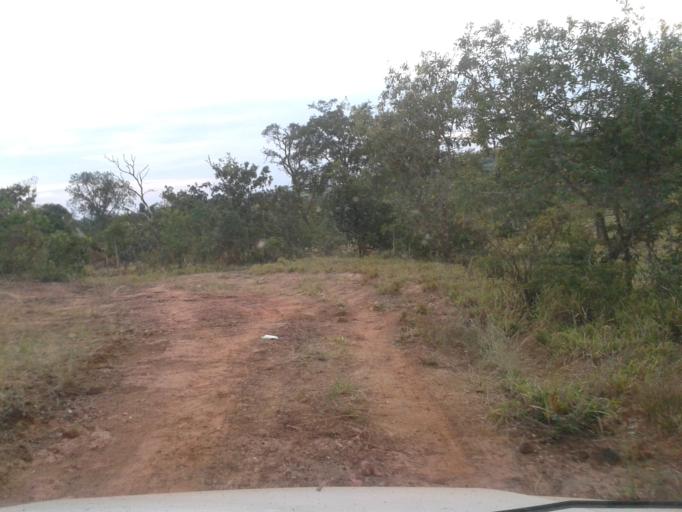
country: BR
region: Minas Gerais
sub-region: Campina Verde
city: Campina Verde
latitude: -19.4138
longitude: -49.6161
